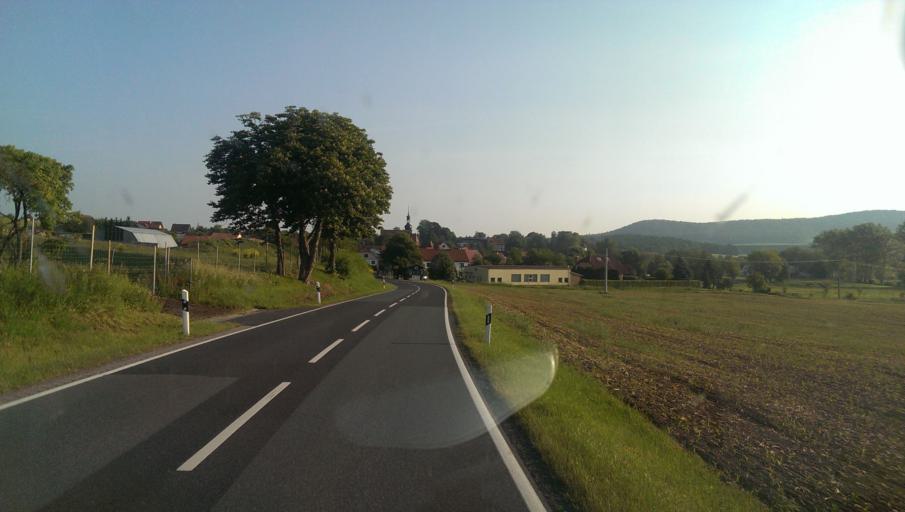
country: DE
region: Thuringia
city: Wolfershausen
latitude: 50.4644
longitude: 10.4380
